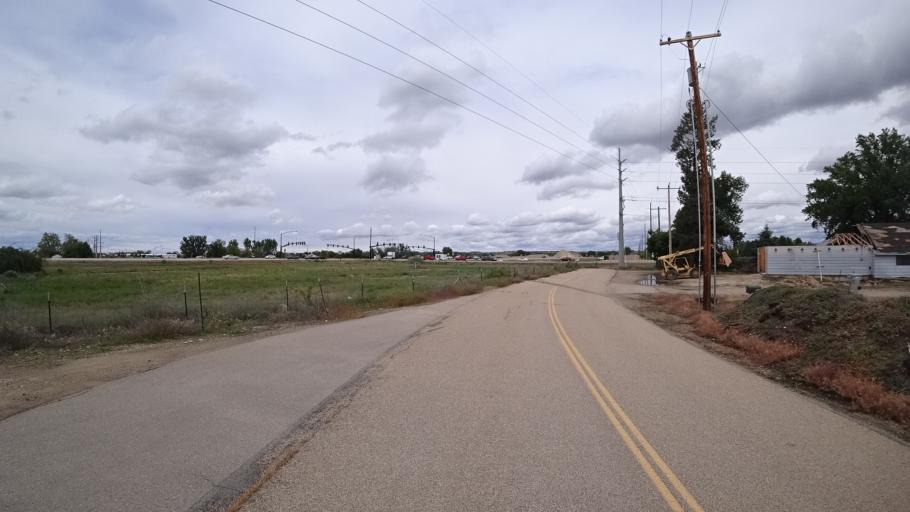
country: US
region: Idaho
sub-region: Ada County
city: Star
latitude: 43.6907
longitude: -116.4585
